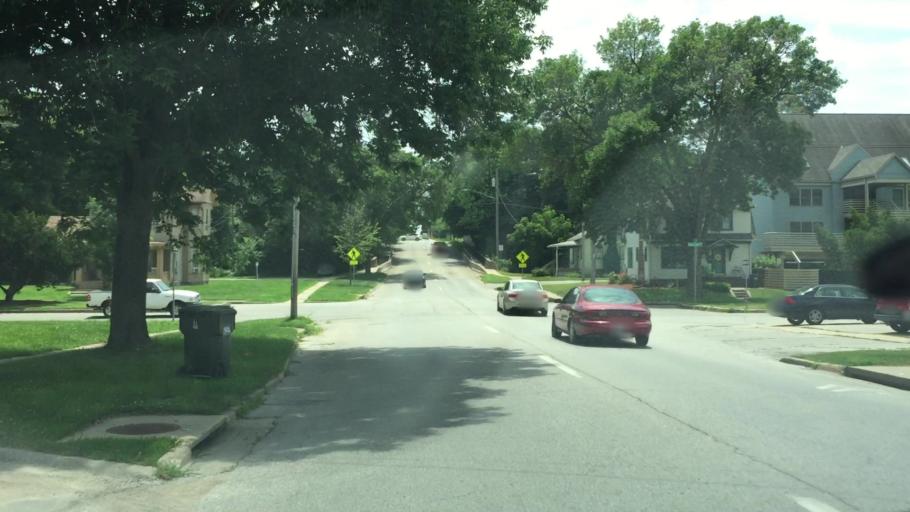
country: US
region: Iowa
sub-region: Johnson County
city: Iowa City
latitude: 41.6616
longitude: -91.5258
